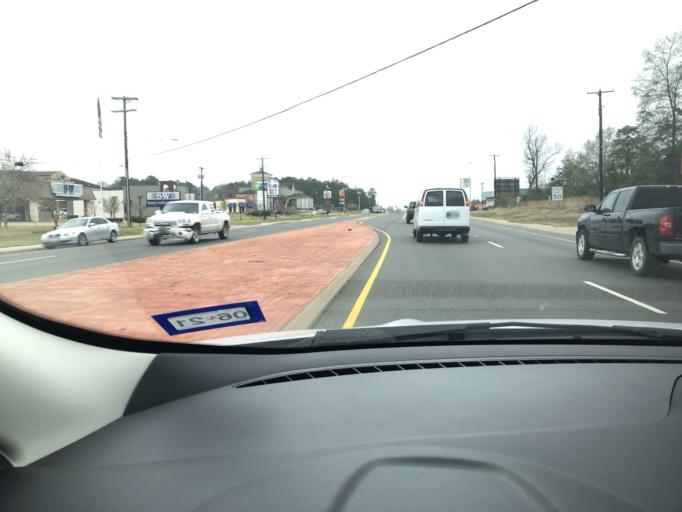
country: US
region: Texas
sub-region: Nacogdoches County
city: Nacogdoches
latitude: 31.5724
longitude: -94.6745
